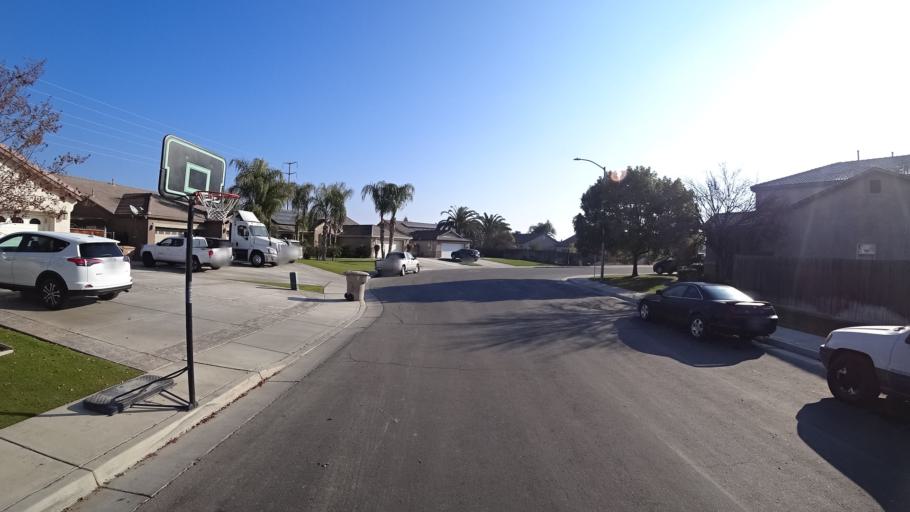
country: US
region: California
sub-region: Kern County
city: Greenacres
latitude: 35.3103
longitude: -119.1269
